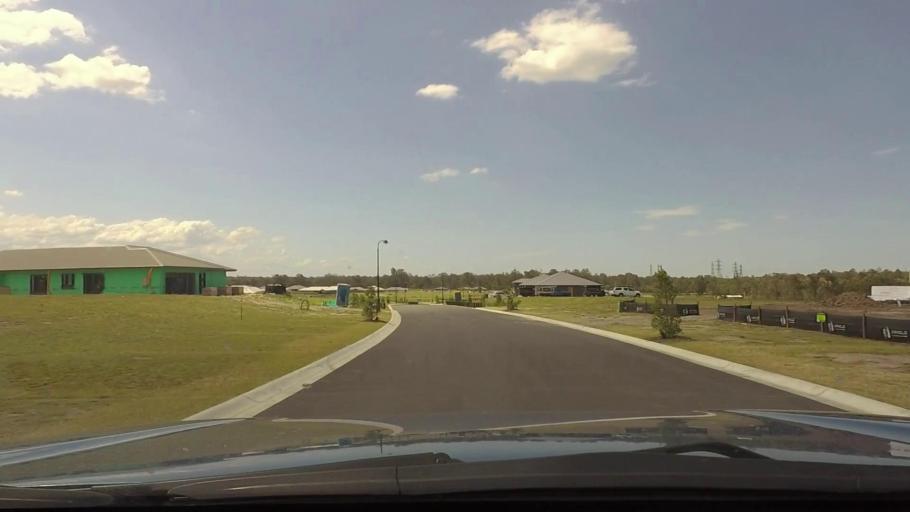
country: AU
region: Queensland
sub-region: Logan
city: North Maclean
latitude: -27.7406
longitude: 152.9511
